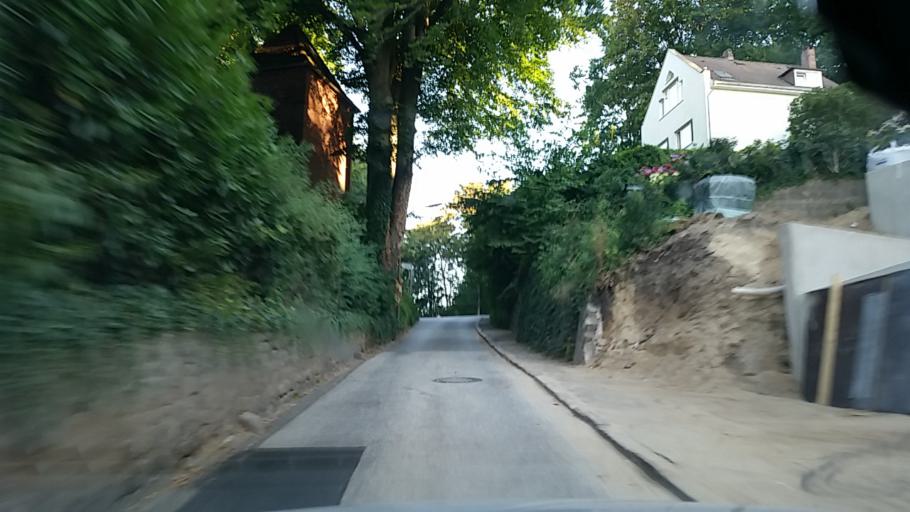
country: DE
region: Schleswig-Holstein
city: Halstenbek
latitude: 53.5613
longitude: 9.7988
